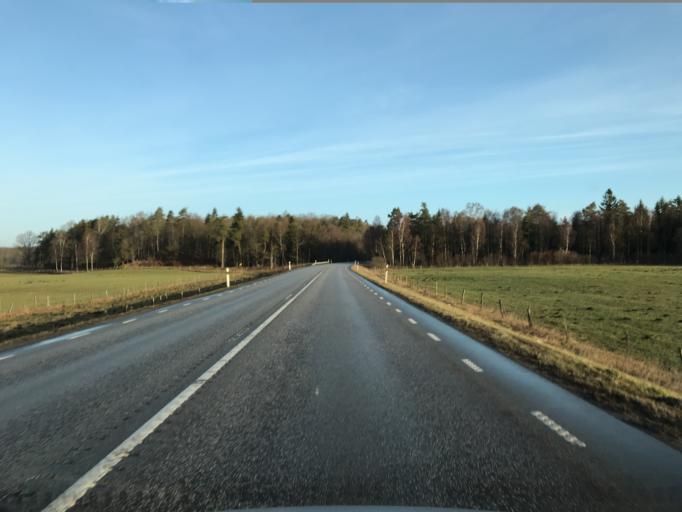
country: SE
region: Skane
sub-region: Hassleholms Kommun
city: Bjarnum
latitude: 56.2580
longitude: 13.7178
